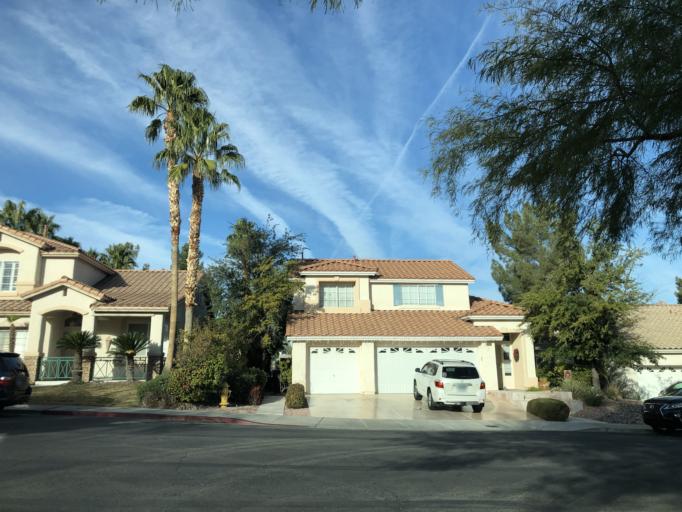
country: US
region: Nevada
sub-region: Clark County
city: Whitney
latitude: 36.0225
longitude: -115.0744
